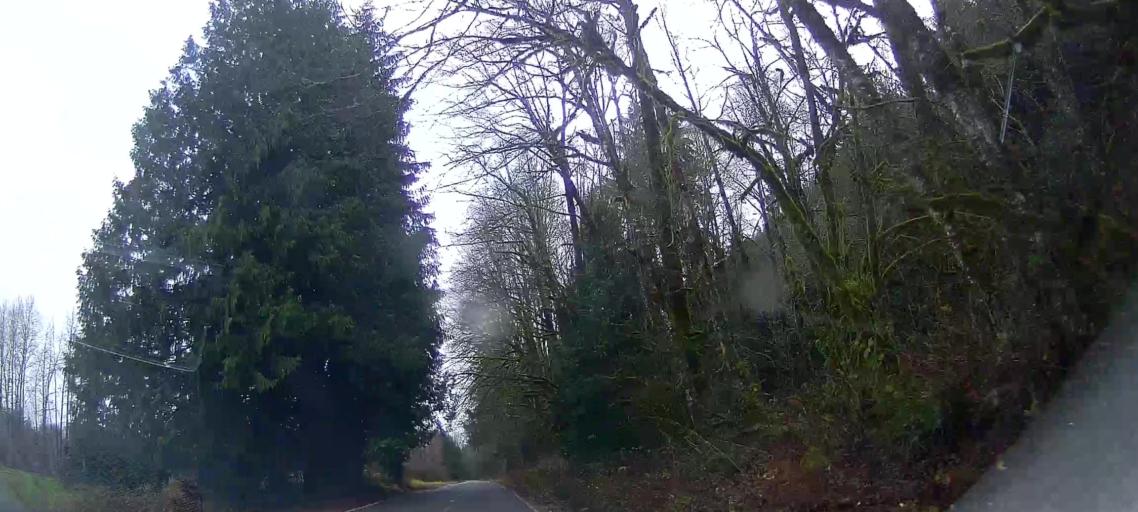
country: US
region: Washington
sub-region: Skagit County
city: Sedro-Woolley
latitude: 48.5138
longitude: -121.9421
